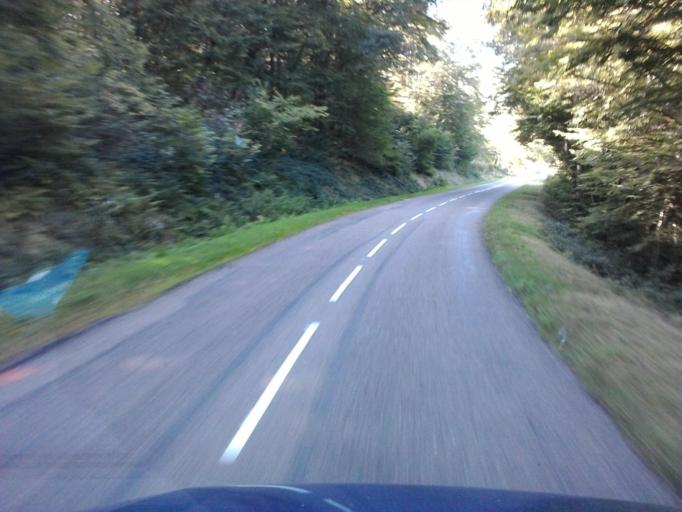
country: FR
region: Bourgogne
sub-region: Departement de la Nievre
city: Lormes
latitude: 47.2152
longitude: 3.9366
